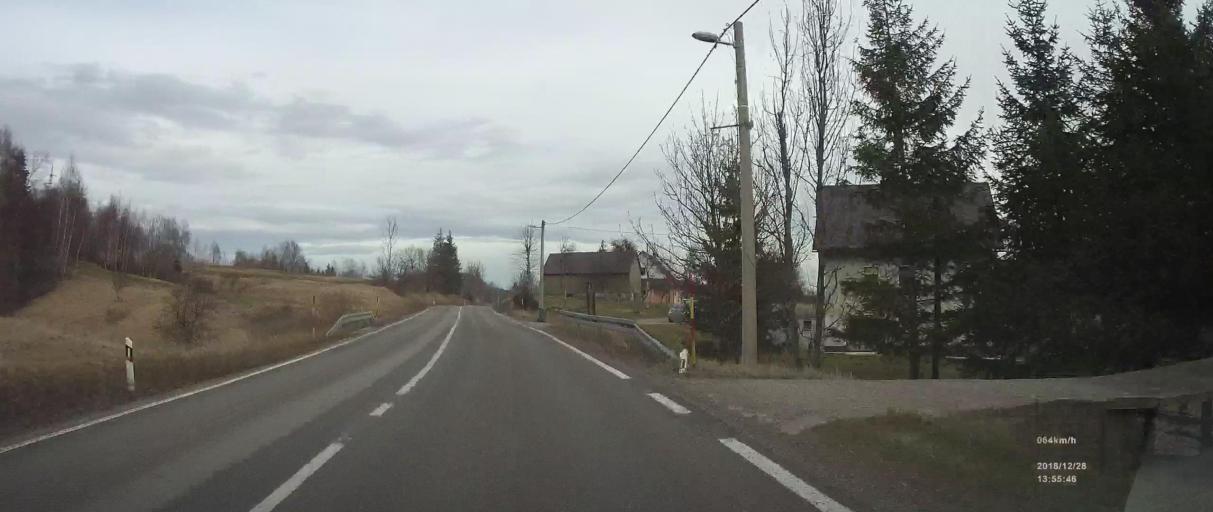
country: HR
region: Primorsko-Goranska
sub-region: Grad Delnice
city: Delnice
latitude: 45.3835
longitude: 14.8803
